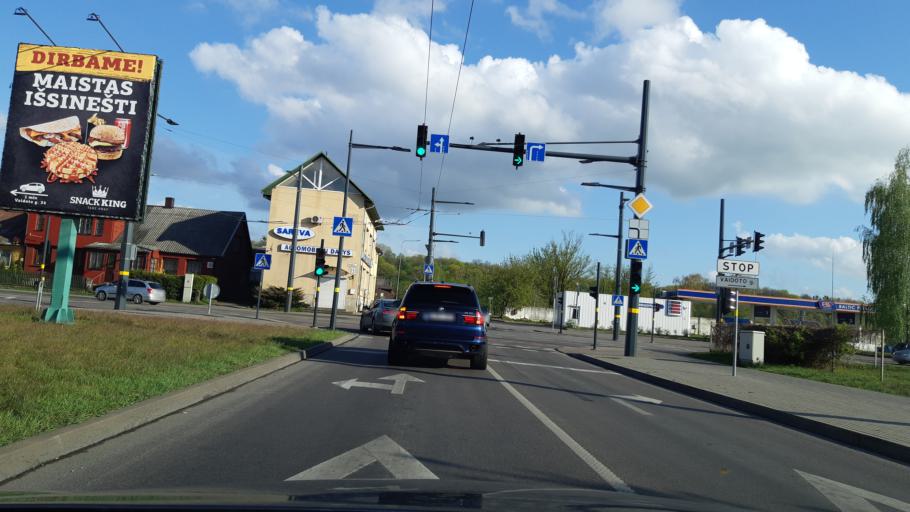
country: LT
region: Kauno apskritis
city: Dainava (Kaunas)
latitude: 54.8622
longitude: 23.9583
